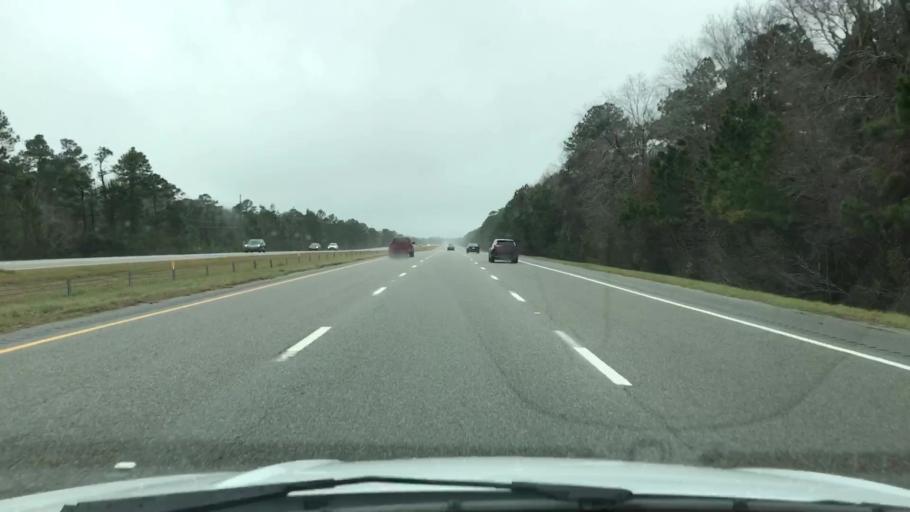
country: US
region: South Carolina
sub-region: Horry County
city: Forestbrook
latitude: 33.7490
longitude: -78.9051
